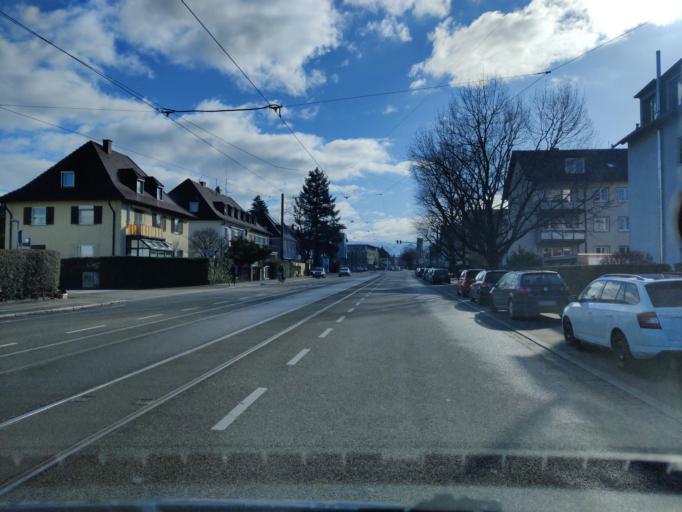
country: DE
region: Baden-Wuerttemberg
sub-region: Freiburg Region
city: Freiburg
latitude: 47.9854
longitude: 7.8916
